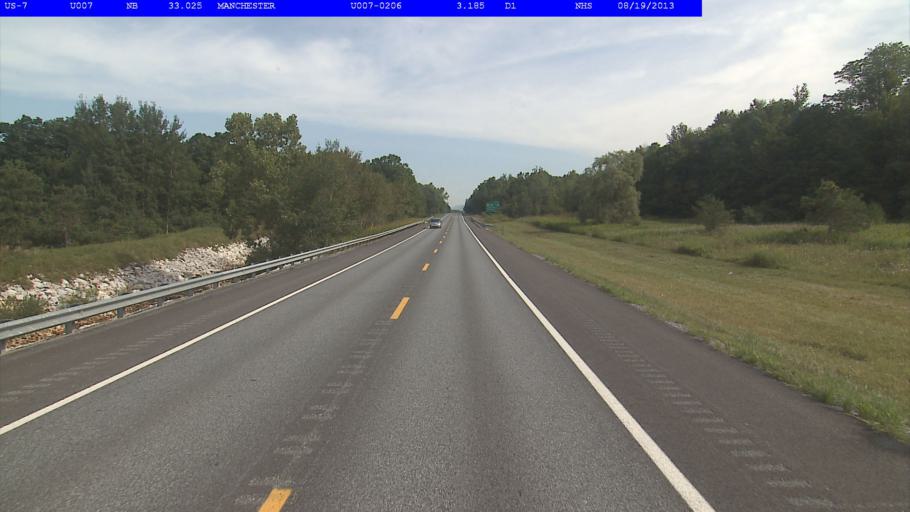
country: US
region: Vermont
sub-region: Bennington County
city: Manchester Center
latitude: 43.1553
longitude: -73.0448
